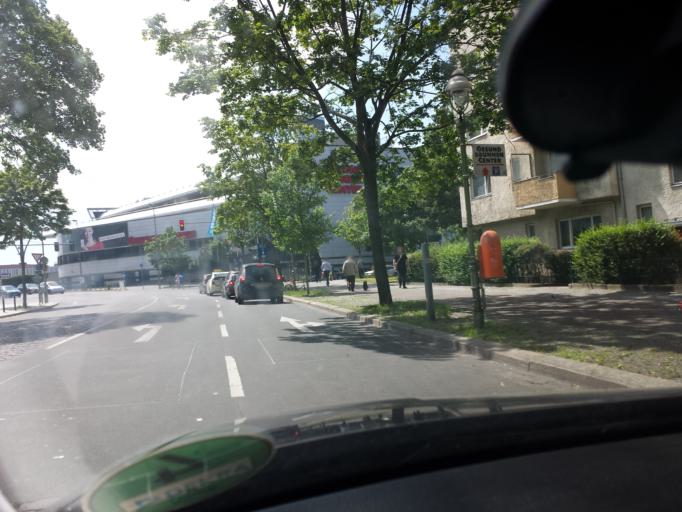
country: DE
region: Berlin
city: Gesundbrunnen
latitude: 52.5509
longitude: 13.3913
